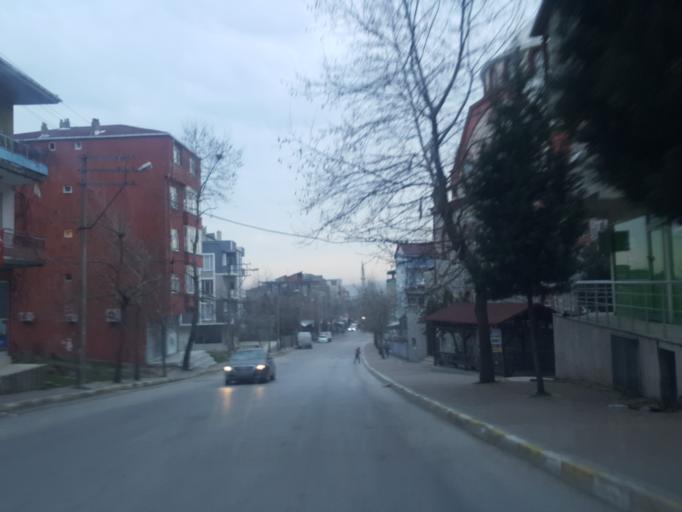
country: TR
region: Kocaeli
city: Tavsancil
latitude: 40.7906
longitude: 29.5446
